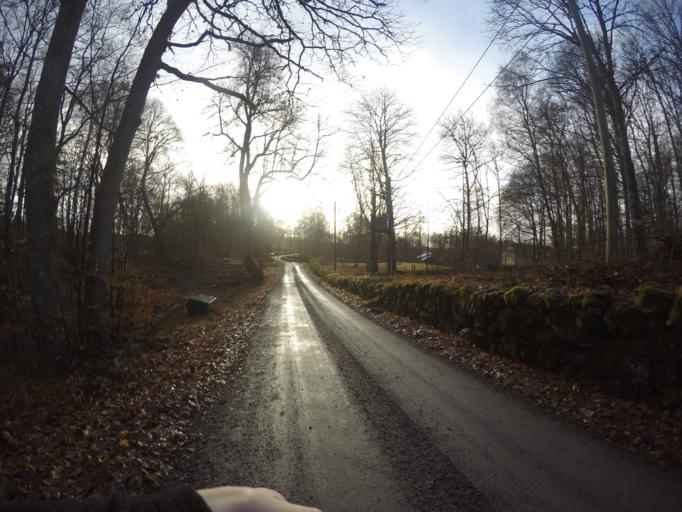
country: SE
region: Skane
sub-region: Osby Kommun
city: Lonsboda
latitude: 56.3718
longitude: 14.3373
